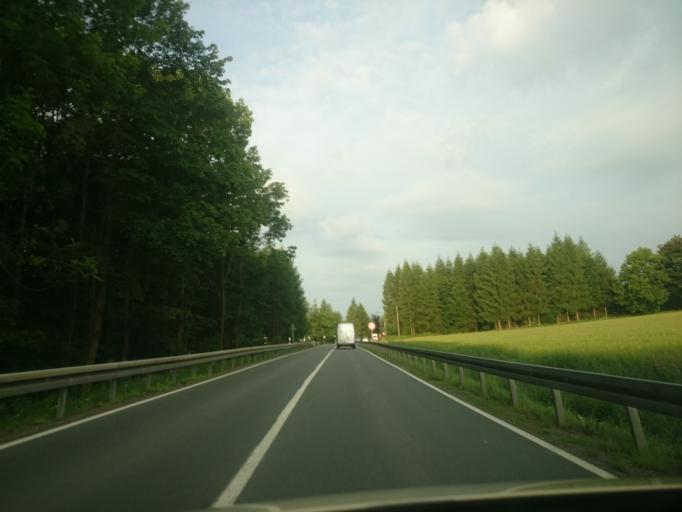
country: DE
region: Saxony
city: Grossolbersdorf
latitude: 50.6832
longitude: 13.1264
